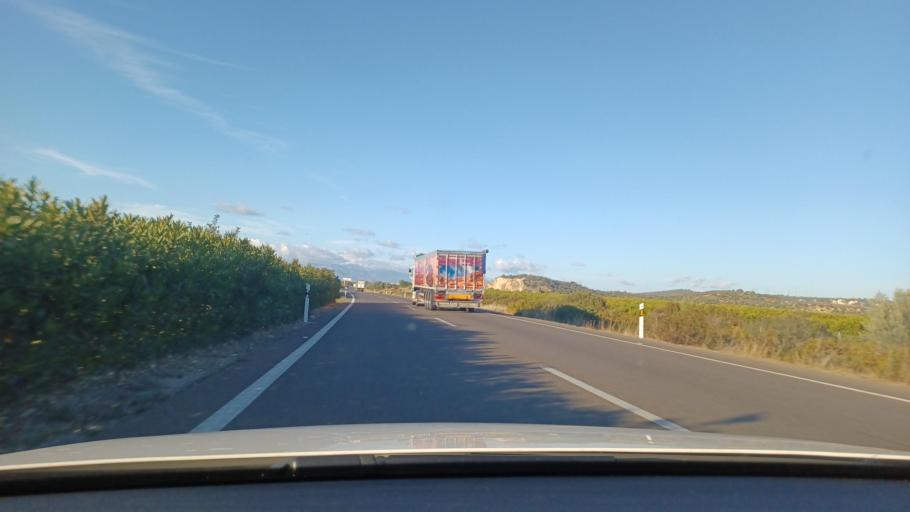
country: ES
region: Valencia
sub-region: Provincia de Castello
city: Vinaros
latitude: 40.4800
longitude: 0.4179
